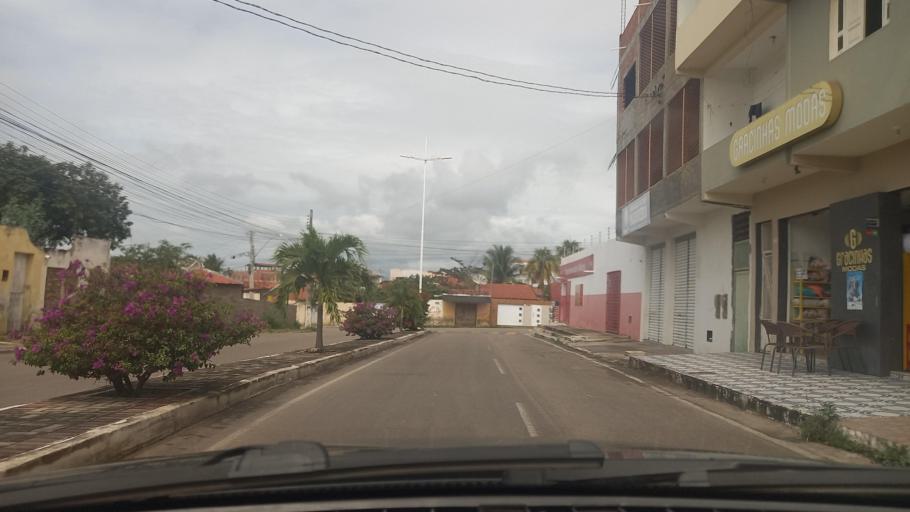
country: BR
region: Bahia
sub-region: Paulo Afonso
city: Paulo Afonso
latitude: -9.4380
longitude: -38.2118
